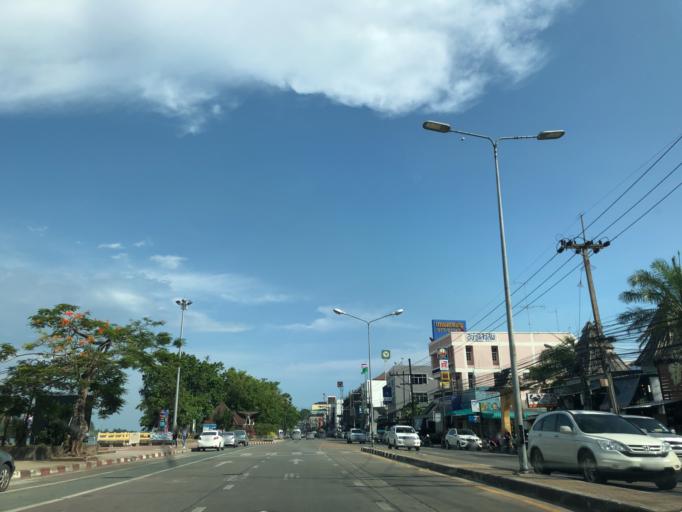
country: TH
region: Krabi
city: Krabi
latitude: 8.0675
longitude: 98.9169
